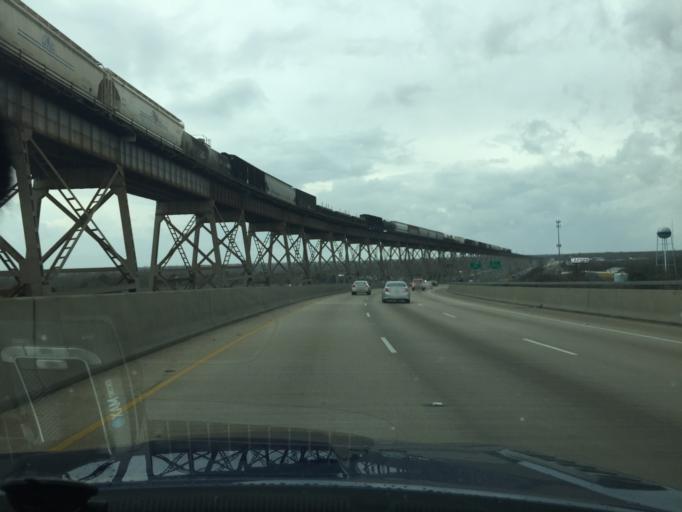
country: US
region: Louisiana
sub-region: Jefferson Parish
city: Bridge City
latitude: 29.9375
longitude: -90.1632
